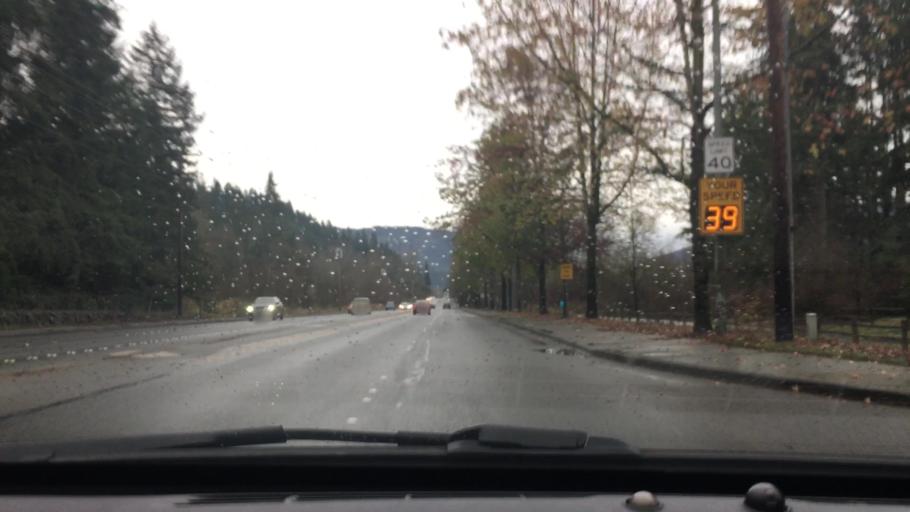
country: US
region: Washington
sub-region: King County
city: Issaquah
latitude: 47.5649
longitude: -122.0523
